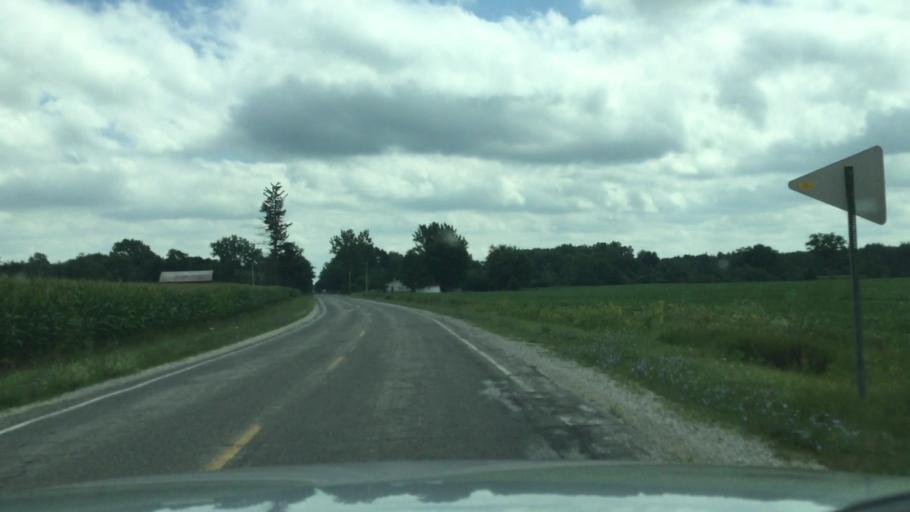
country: US
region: Michigan
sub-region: Saginaw County
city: Birch Run
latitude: 43.2935
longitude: -83.8154
